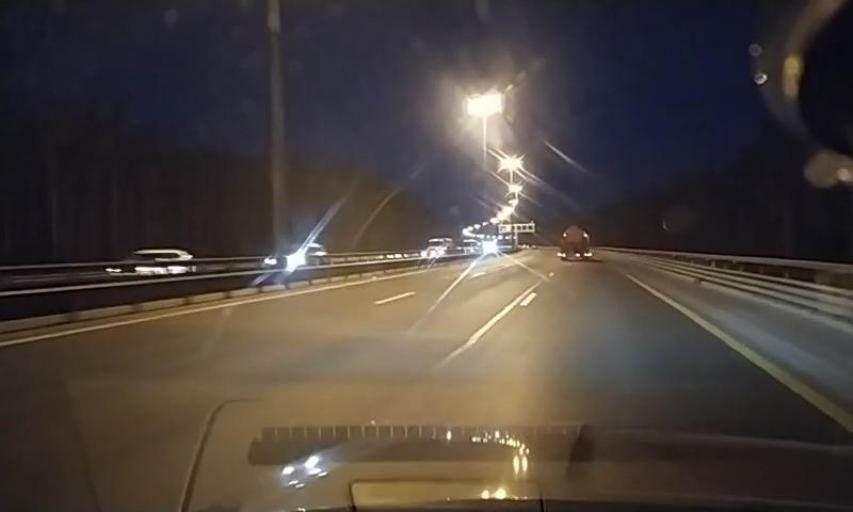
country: RU
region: St.-Petersburg
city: Pesochnyy
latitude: 60.0770
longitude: 30.1271
